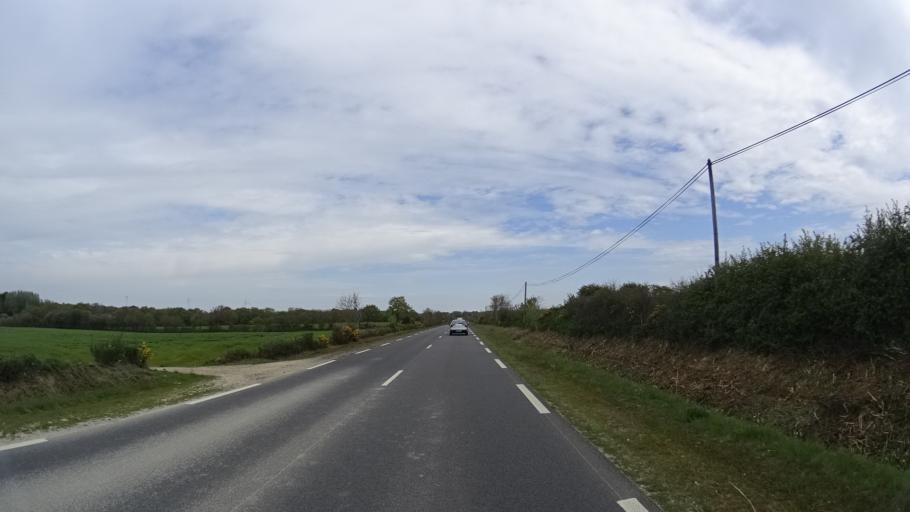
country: FR
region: Pays de la Loire
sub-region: Departement de la Loire-Atlantique
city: Bourgneuf-en-Retz
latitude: 47.0508
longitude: -1.9314
